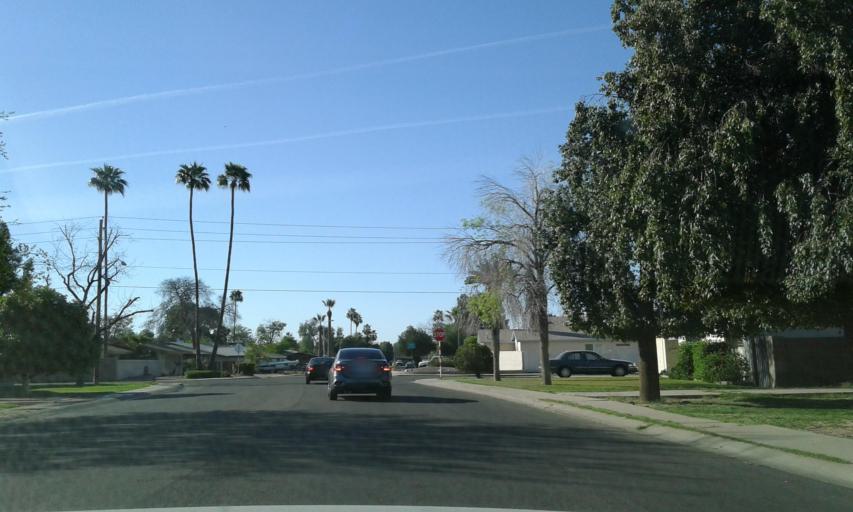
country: US
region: Arizona
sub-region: Maricopa County
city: Glendale
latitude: 33.5428
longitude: -112.1079
